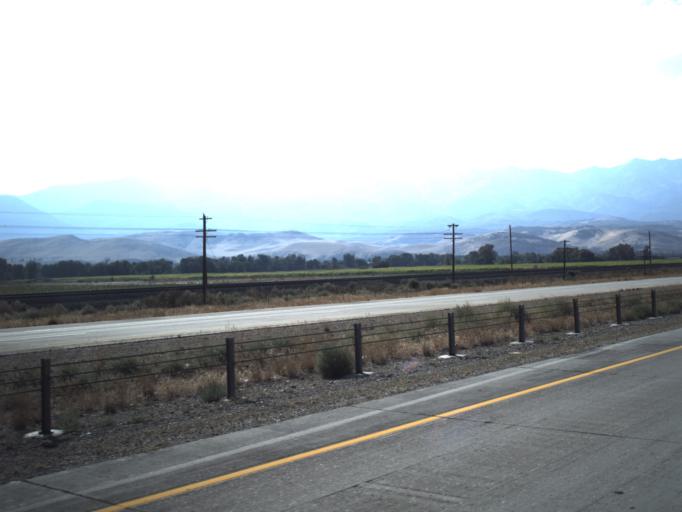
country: US
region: Utah
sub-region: Morgan County
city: Morgan
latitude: 41.0518
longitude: -111.6856
